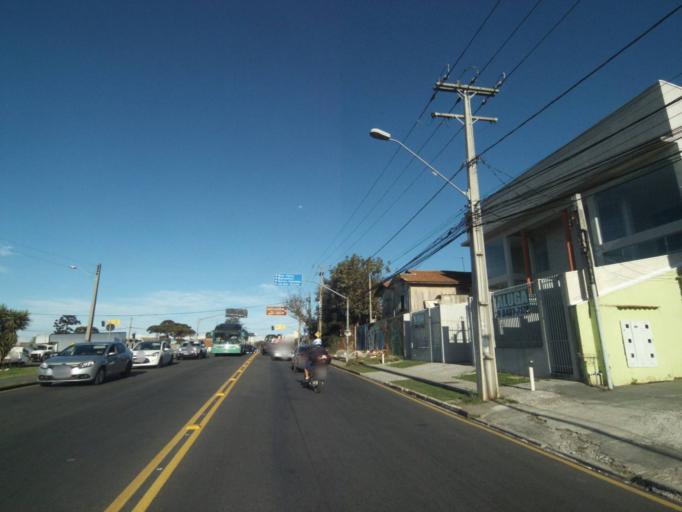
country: BR
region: Parana
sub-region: Curitiba
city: Curitiba
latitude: -25.3903
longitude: -49.2595
